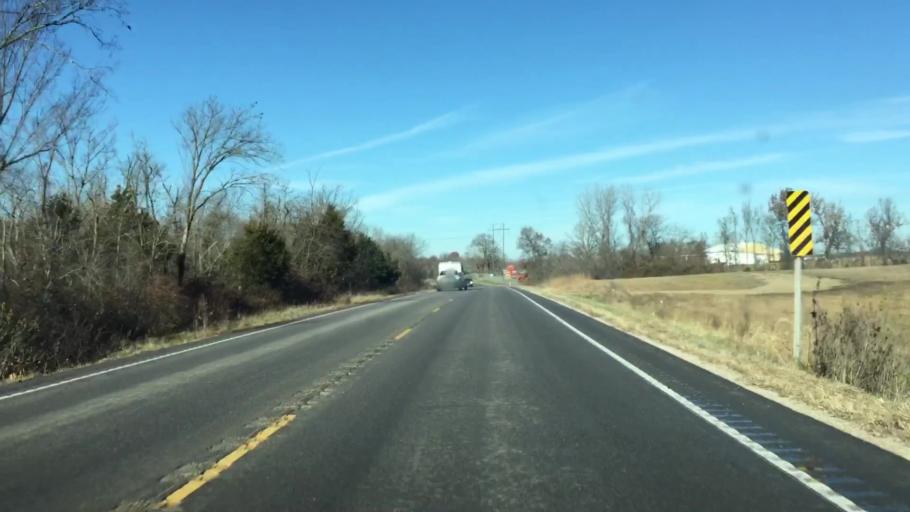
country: US
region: Missouri
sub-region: Miller County
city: Eldon
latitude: 38.3597
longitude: -92.6043
